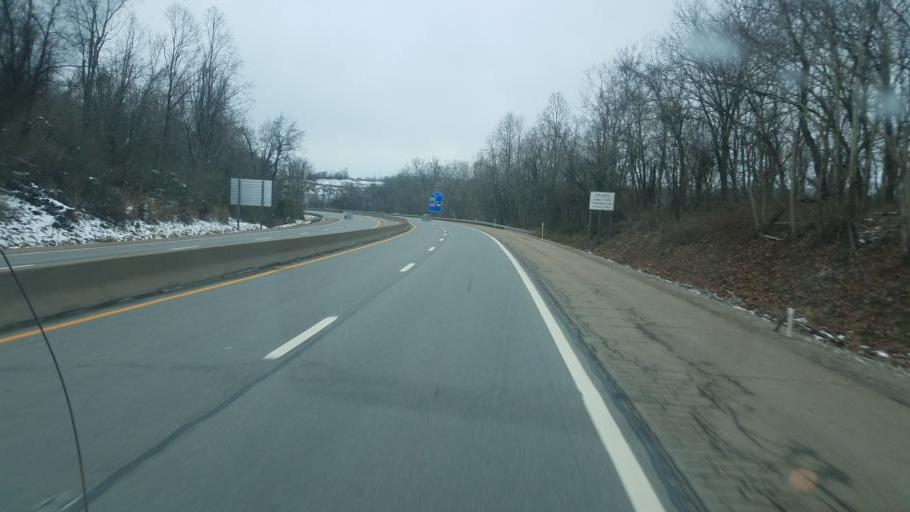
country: US
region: West Virginia
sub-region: Wood County
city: Williamstown
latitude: 39.3957
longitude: -81.4379
